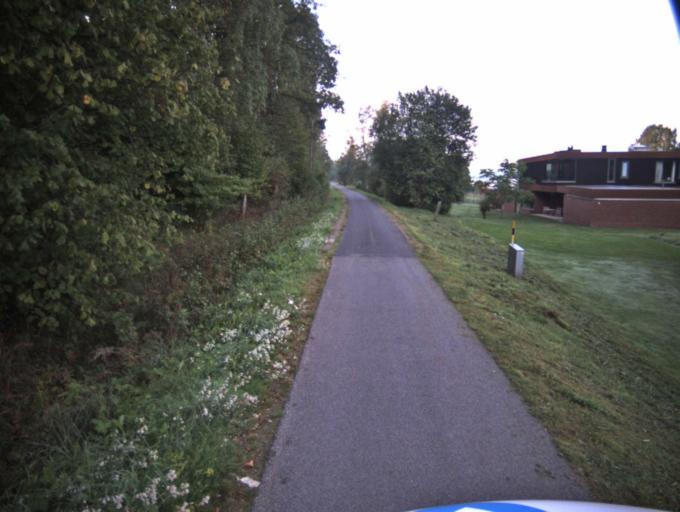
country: SE
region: Vaestra Goetaland
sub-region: Ulricehamns Kommun
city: Ulricehamn
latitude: 57.7659
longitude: 13.4001
